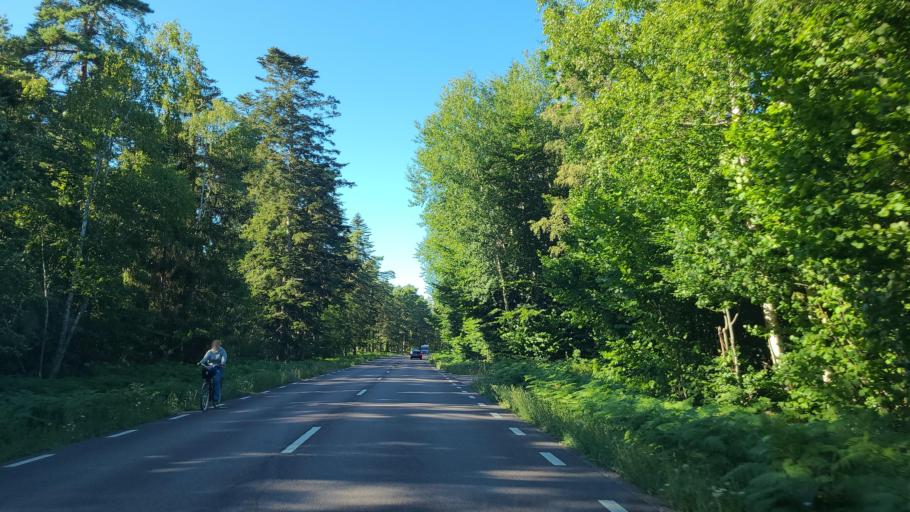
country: SE
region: Kalmar
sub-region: Borgholms Kommun
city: Borgholm
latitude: 57.2848
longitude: 17.0206
